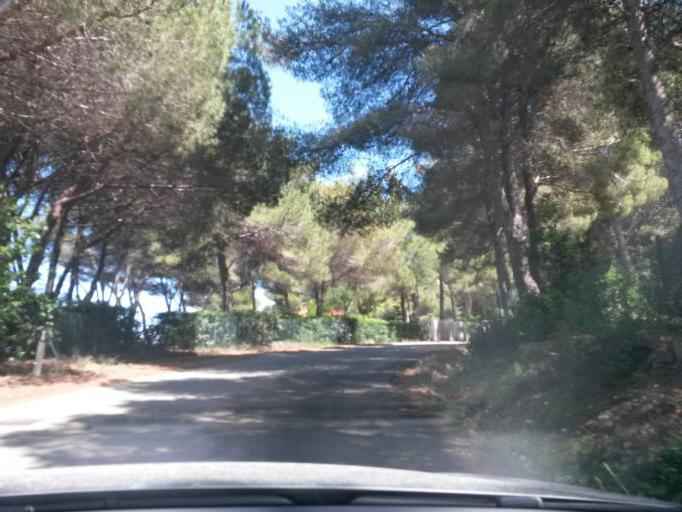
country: IT
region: Tuscany
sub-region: Provincia di Livorno
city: Rio Marina
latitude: 42.8568
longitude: 10.4275
